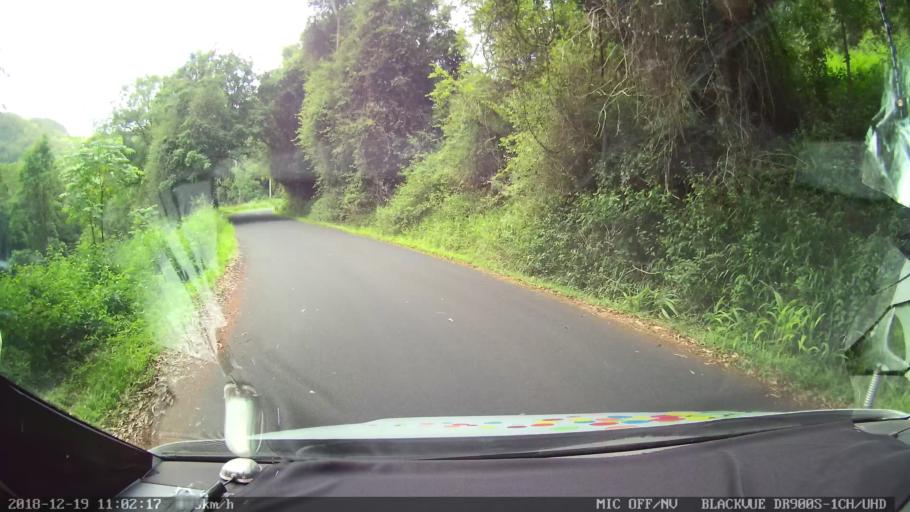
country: AU
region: New South Wales
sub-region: Lismore Municipality
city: Nimbin
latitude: -28.6064
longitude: 153.2667
